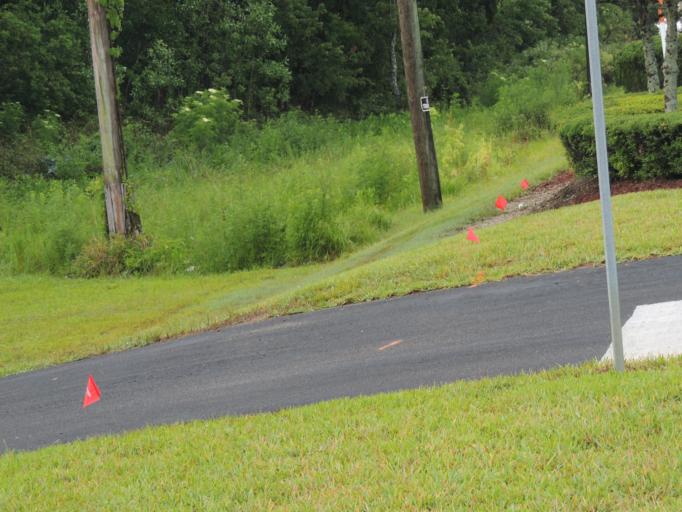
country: US
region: Florida
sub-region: Osceola County
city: Kissimmee
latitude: 28.3229
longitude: -81.4706
